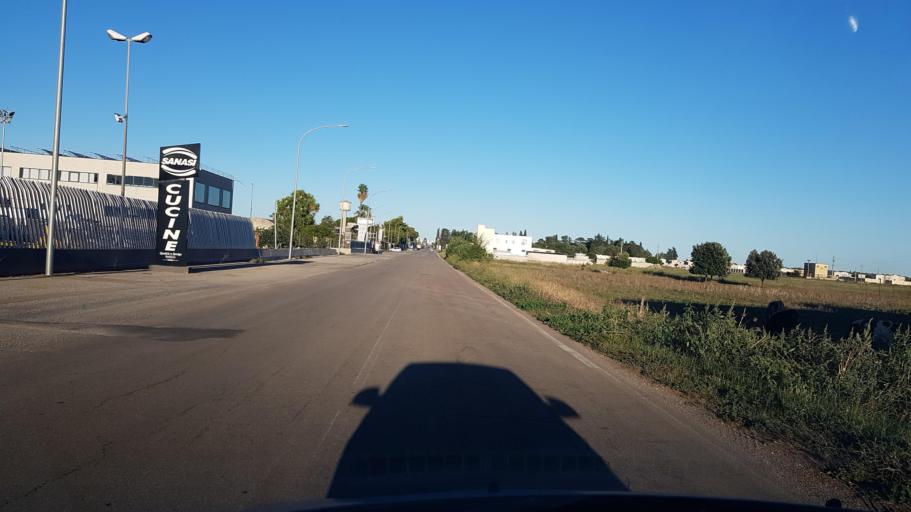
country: IT
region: Apulia
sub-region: Provincia di Brindisi
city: San Pancrazio Salentino
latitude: 40.4164
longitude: 17.8144
